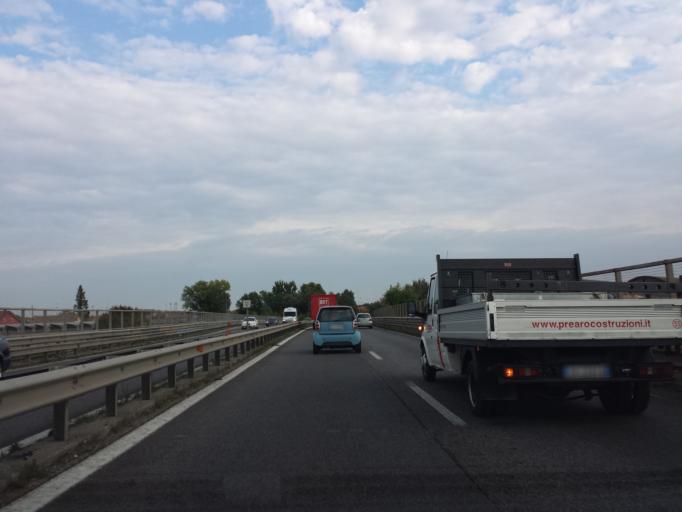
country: IT
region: Veneto
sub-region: Provincia di Padova
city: Mandriola-Sant'Agostino
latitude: 45.3744
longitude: 11.8495
